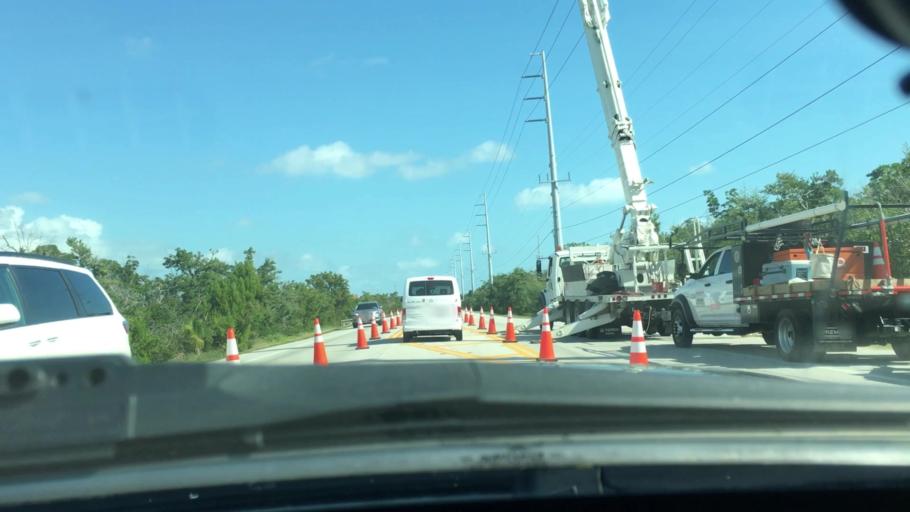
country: US
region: Florida
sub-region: Monroe County
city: Marathon
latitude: 24.7077
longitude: -81.1174
